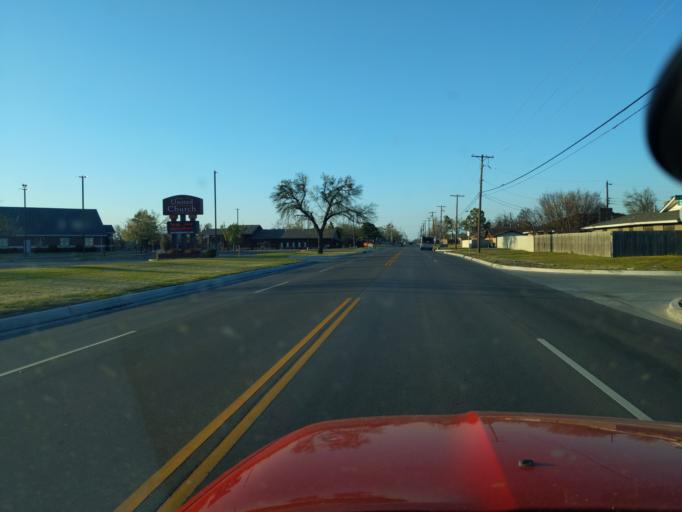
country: US
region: Oklahoma
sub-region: Oklahoma County
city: Oklahoma City
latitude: 35.3998
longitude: -97.5213
